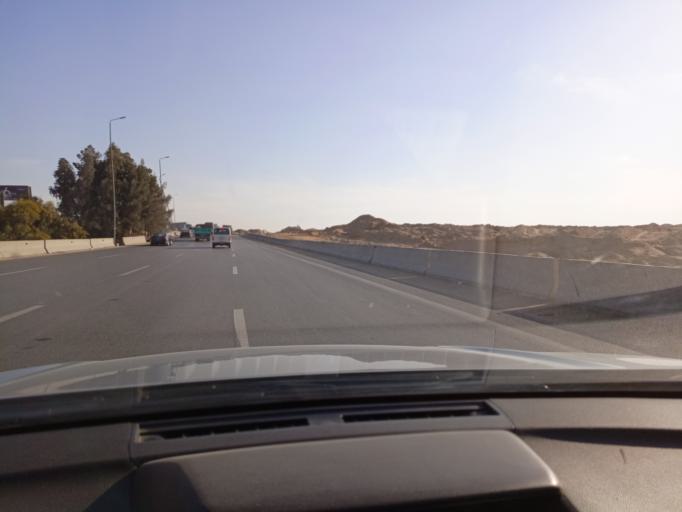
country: EG
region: Muhafazat al Qahirah
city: Cairo
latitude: 30.0240
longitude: 31.4009
